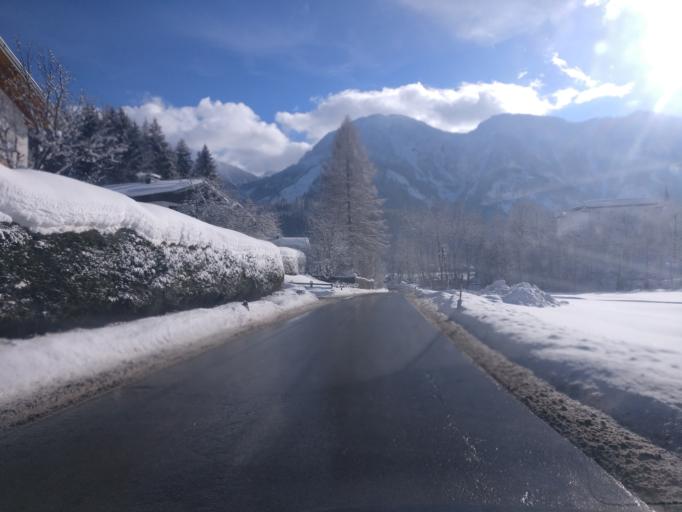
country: AT
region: Salzburg
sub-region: Politischer Bezirk Sankt Johann im Pongau
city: Goldegg
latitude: 47.3217
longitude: 13.1002
